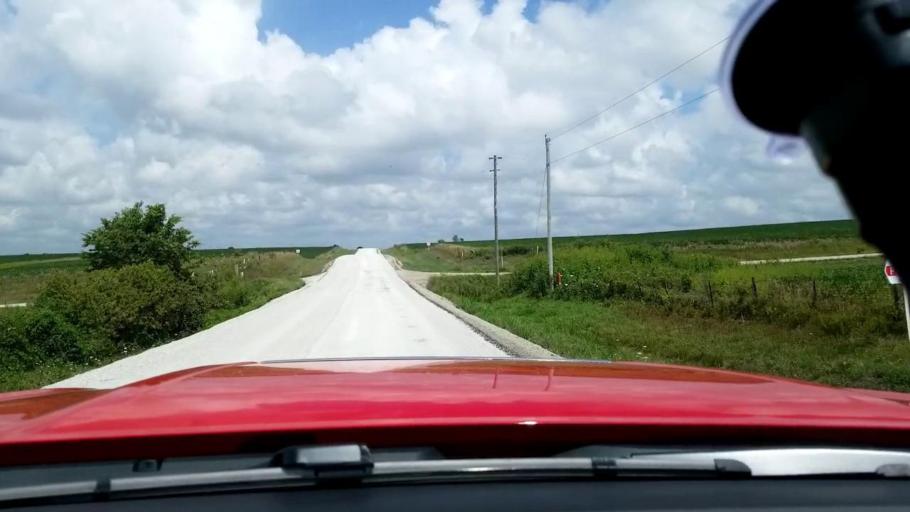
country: US
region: Iowa
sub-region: Decatur County
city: Lamoni
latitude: 40.6668
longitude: -94.0483
